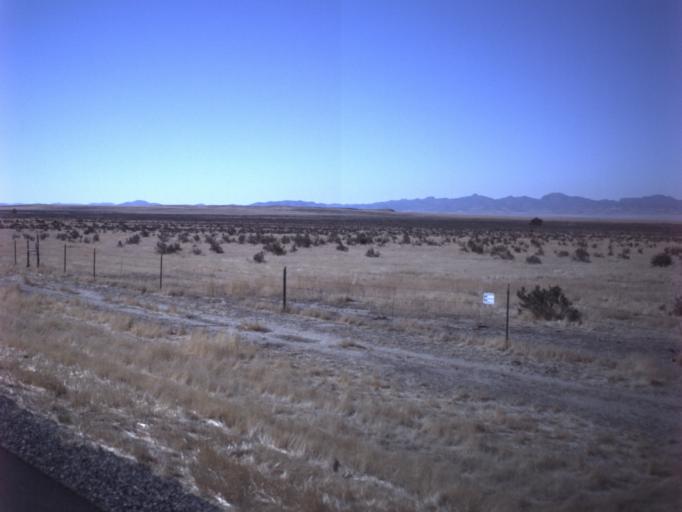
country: US
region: Utah
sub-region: Tooele County
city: Grantsville
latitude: 40.4641
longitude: -112.7470
